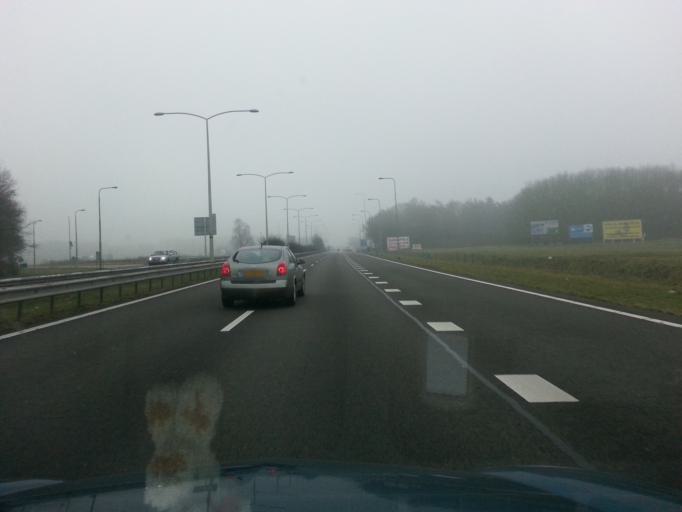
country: NL
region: Gelderland
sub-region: Gemeente Zevenaar
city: Zevenaar
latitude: 51.9027
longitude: 6.1613
